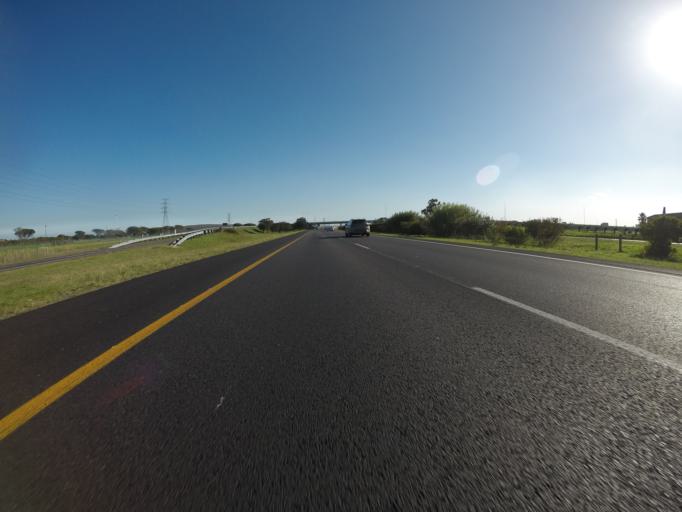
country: ZA
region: Western Cape
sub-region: Cape Winelands District Municipality
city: Stellenbosch
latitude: -34.0593
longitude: 18.7843
